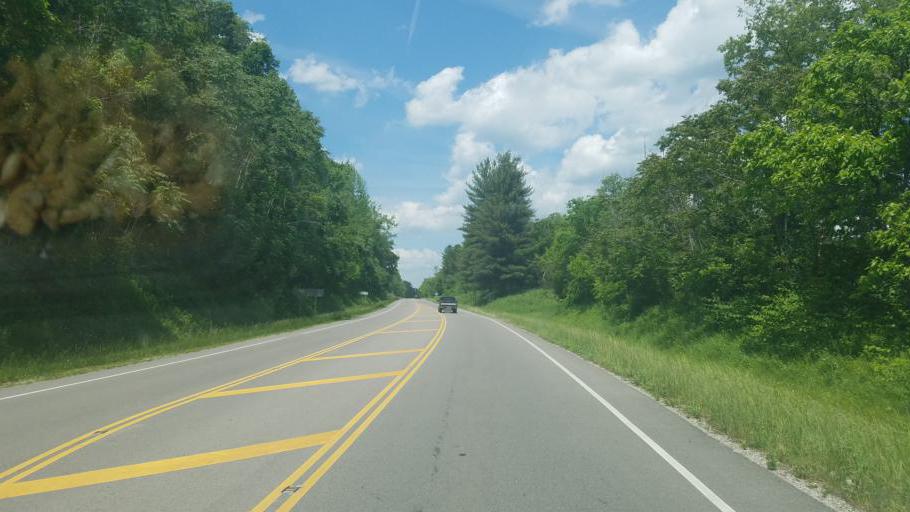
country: US
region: Ohio
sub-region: Meigs County
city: Middleport
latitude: 39.0100
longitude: -82.0684
